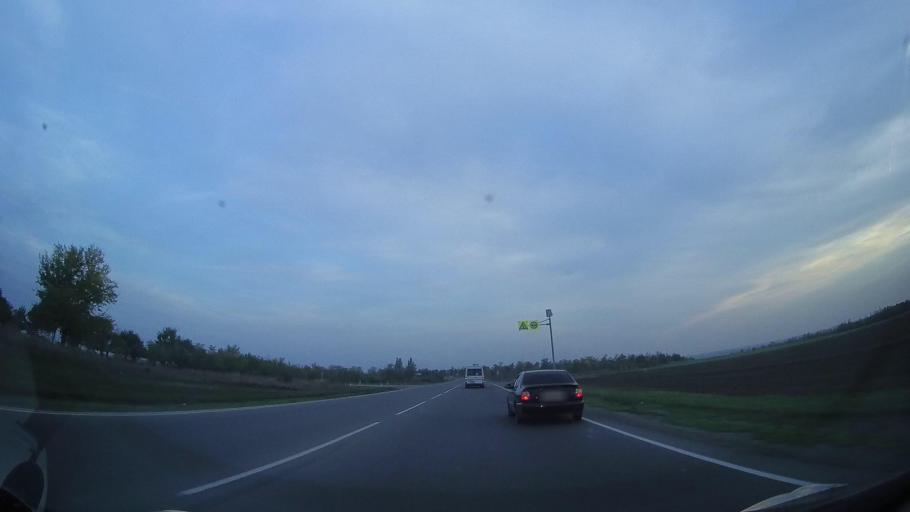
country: RU
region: Rostov
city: Kagal'nitskaya
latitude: 46.8935
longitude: 40.1291
